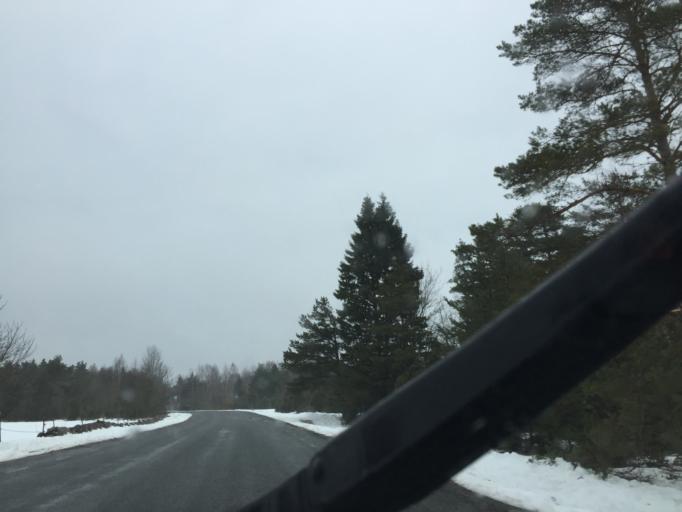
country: EE
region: Saare
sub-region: Kuressaare linn
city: Kuressaare
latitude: 58.2975
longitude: 22.0263
